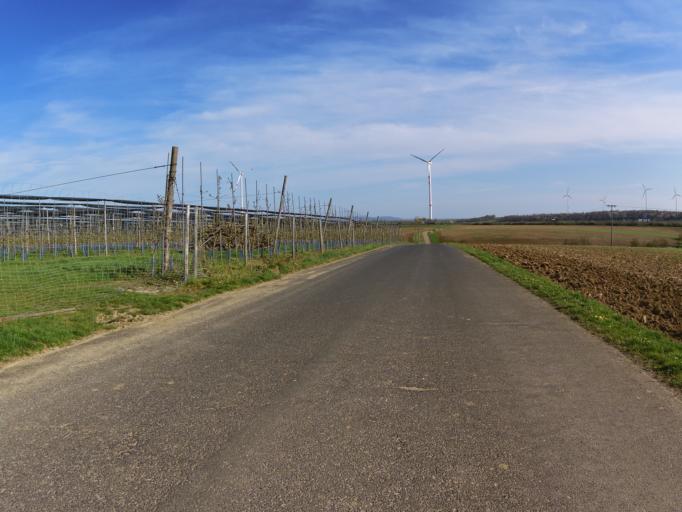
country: DE
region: Bavaria
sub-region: Regierungsbezirk Unterfranken
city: Biebelried
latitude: 49.7894
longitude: 10.1121
